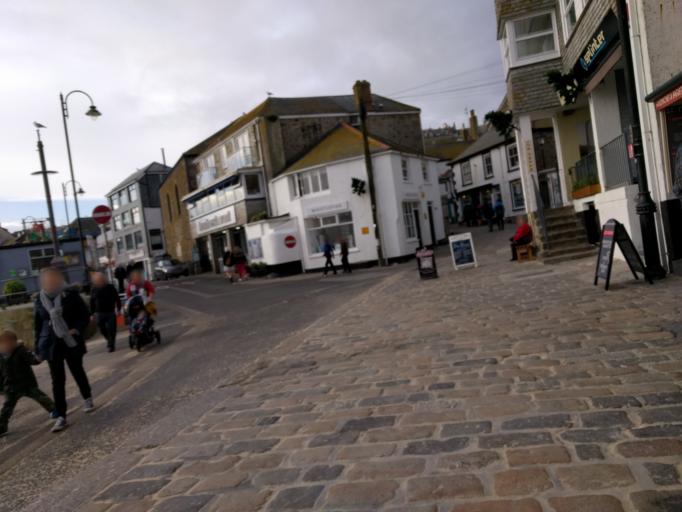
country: GB
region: England
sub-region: Cornwall
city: St Ives
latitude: 50.2150
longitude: -5.4794
